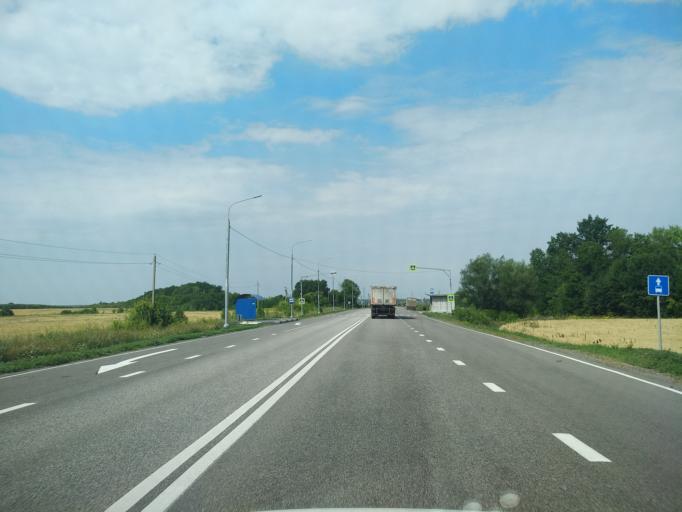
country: RU
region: Voronezj
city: Orlovo
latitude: 51.6757
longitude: 39.7661
